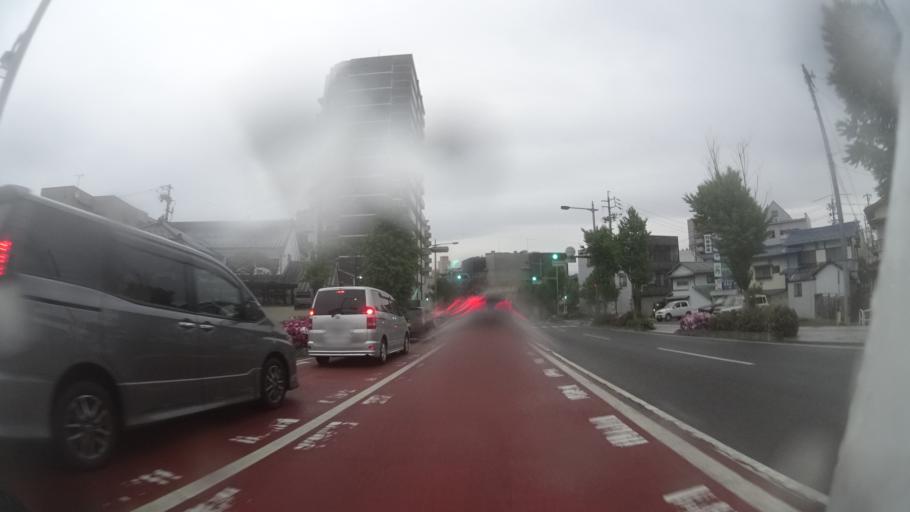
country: JP
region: Nagano
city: Nagano-shi
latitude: 36.6554
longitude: 138.1908
